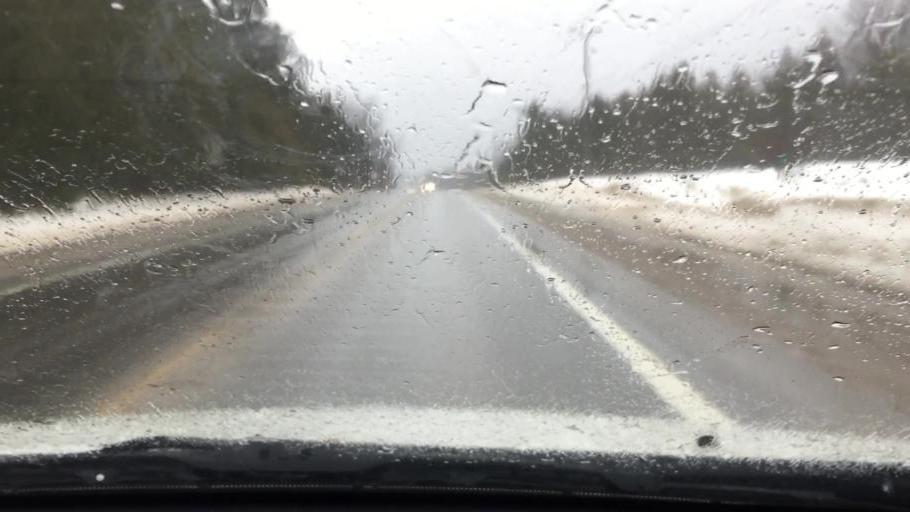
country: US
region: Michigan
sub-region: Charlevoix County
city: Charlevoix
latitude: 45.2723
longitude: -85.2149
